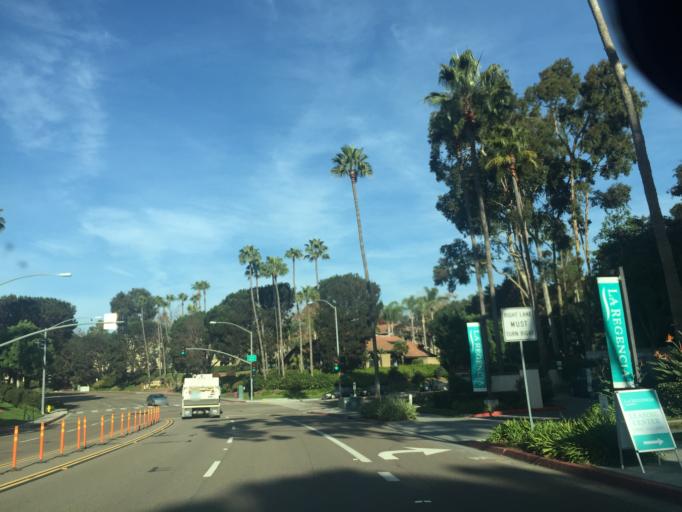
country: US
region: California
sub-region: San Diego County
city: La Jolla
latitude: 32.8645
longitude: -117.2250
